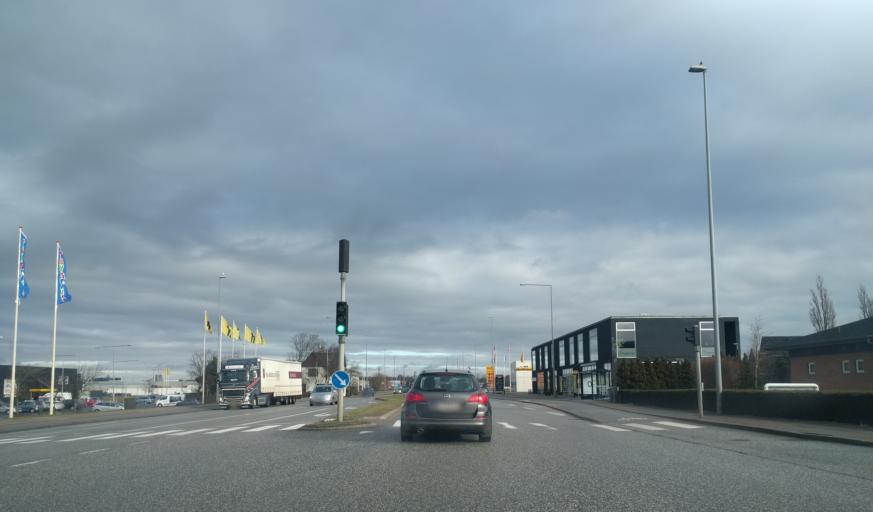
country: DK
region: North Denmark
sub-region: Alborg Kommune
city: Svenstrup
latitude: 57.0000
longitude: 9.8748
